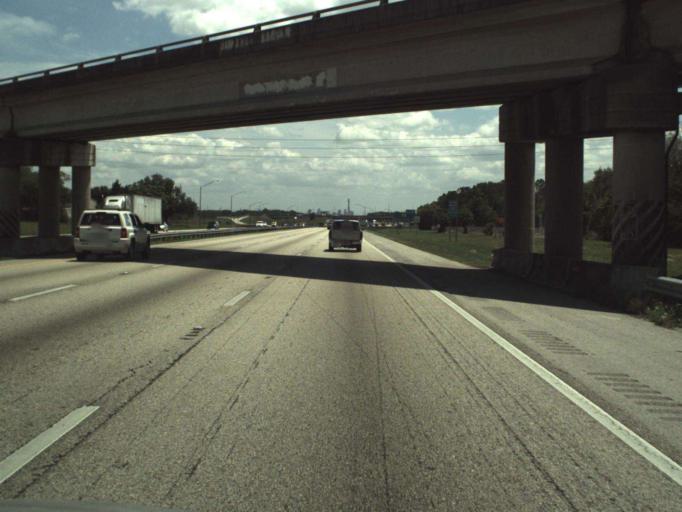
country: US
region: Florida
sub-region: Orange County
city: Eatonville
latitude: 28.6414
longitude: -81.3881
